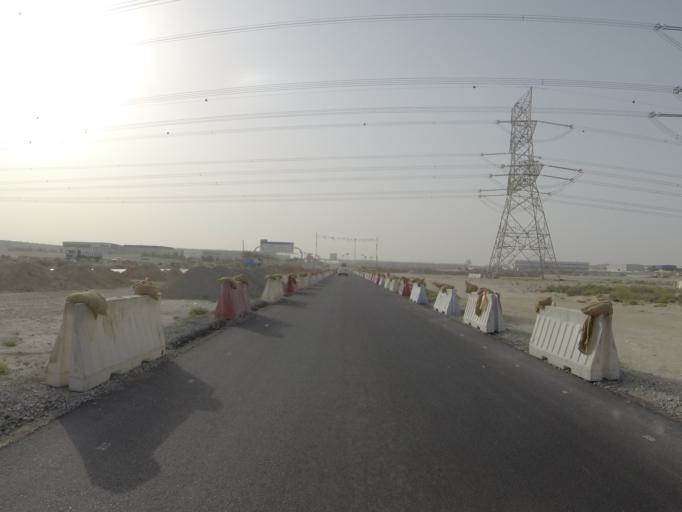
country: AE
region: Dubai
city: Dubai
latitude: 24.9556
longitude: 55.1044
